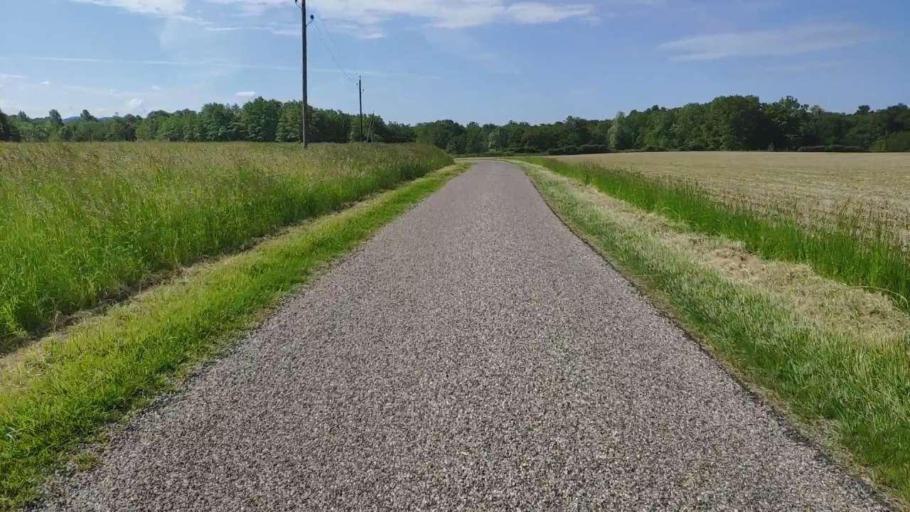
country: FR
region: Franche-Comte
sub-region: Departement du Jura
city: Bletterans
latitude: 46.7038
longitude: 5.4702
